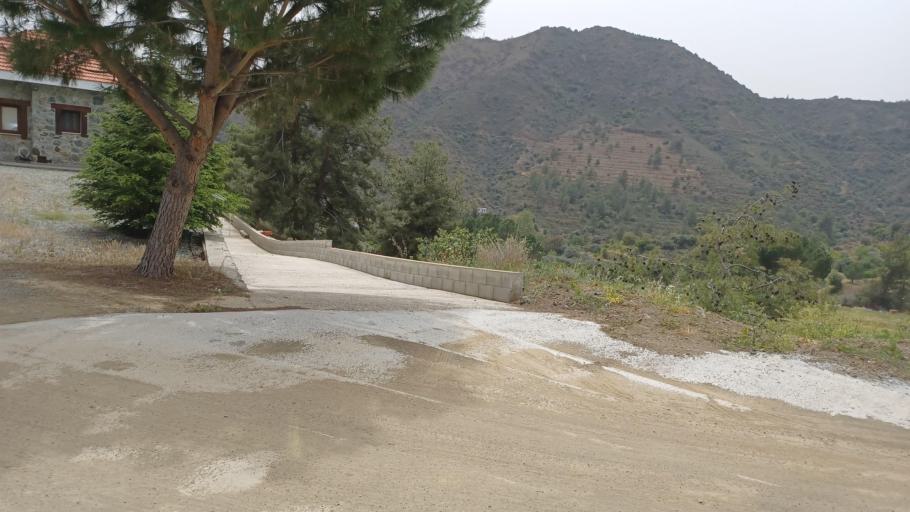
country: CY
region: Limassol
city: Parekklisha
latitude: 34.8480
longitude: 33.1015
